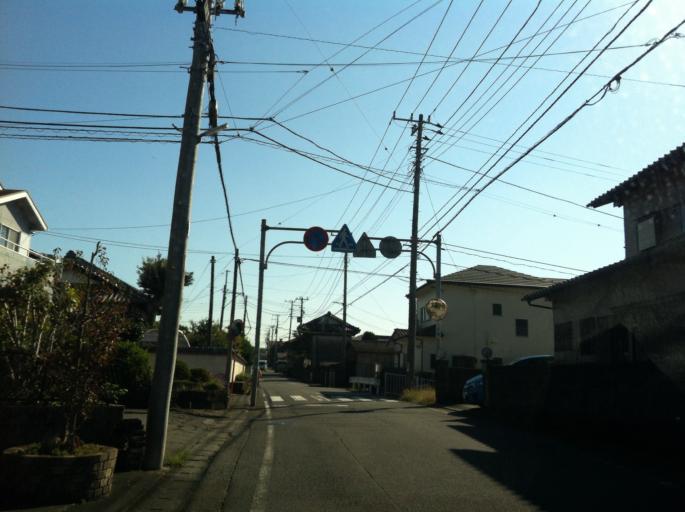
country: JP
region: Shizuoka
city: Fuji
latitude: 35.1552
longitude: 138.7582
